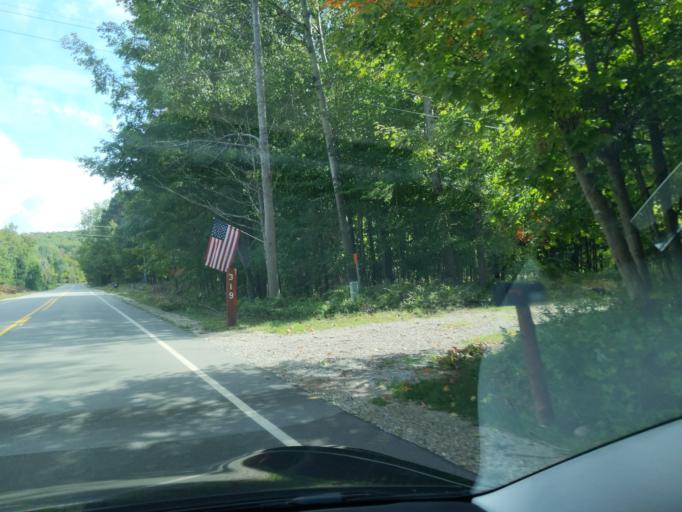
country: US
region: Michigan
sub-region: Antrim County
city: Bellaire
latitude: 45.0402
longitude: -85.3006
